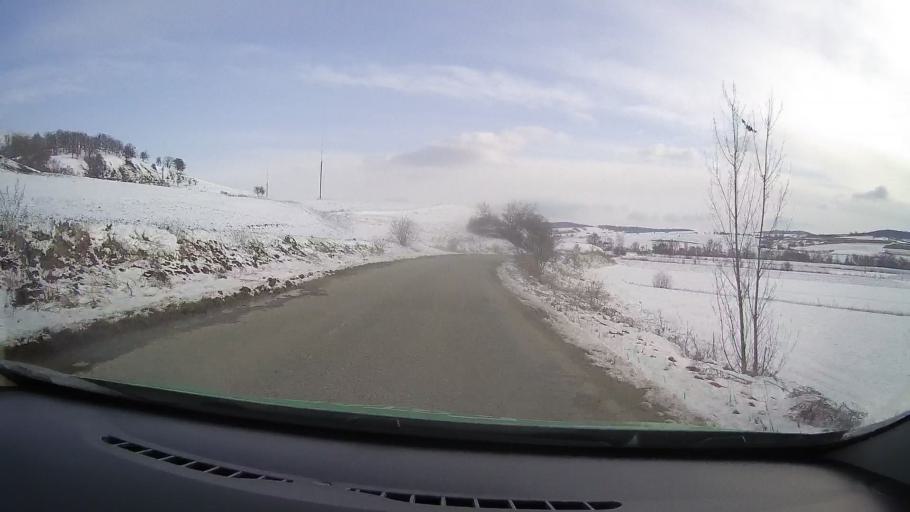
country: RO
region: Sibiu
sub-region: Comuna Merghindeal
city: Merghindeal
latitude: 45.9770
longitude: 24.7057
